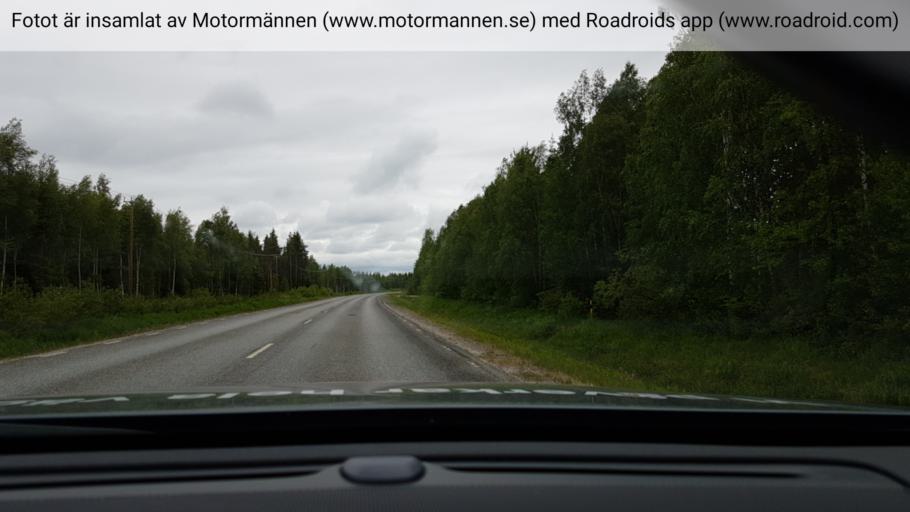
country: SE
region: Vaesterbotten
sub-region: Lycksele Kommun
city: Lycksele
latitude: 64.5541
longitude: 18.5131
